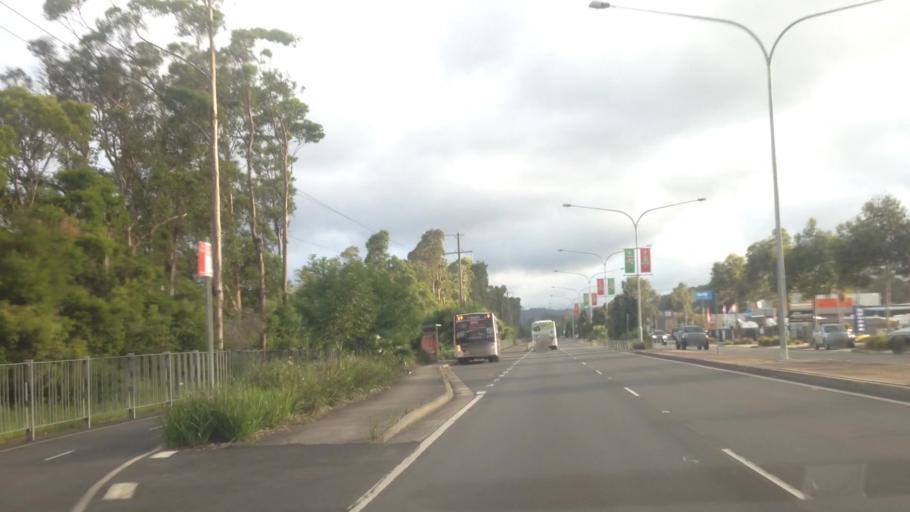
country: AU
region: New South Wales
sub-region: Wyong Shire
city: Chittaway Bay
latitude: -33.3001
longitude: 151.4216
